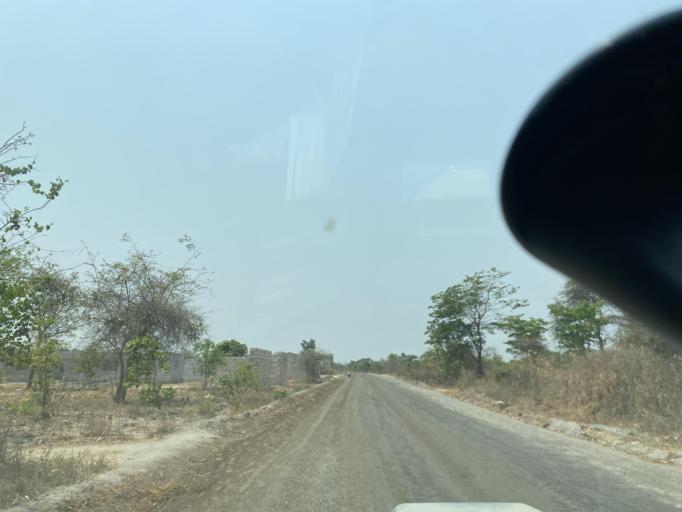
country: ZM
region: Lusaka
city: Lusaka
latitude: -15.5570
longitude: 28.4403
